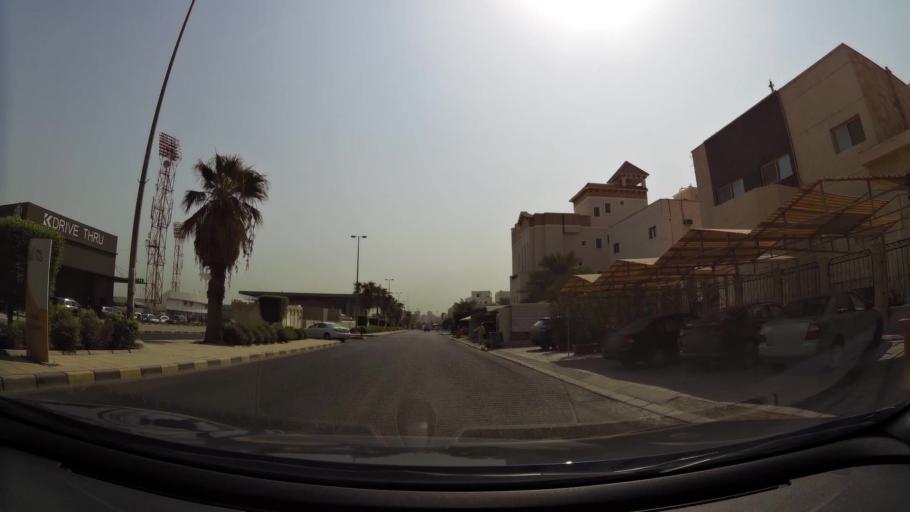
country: KW
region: Al Asimah
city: Ad Dasmah
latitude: 29.3572
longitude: 47.9979
